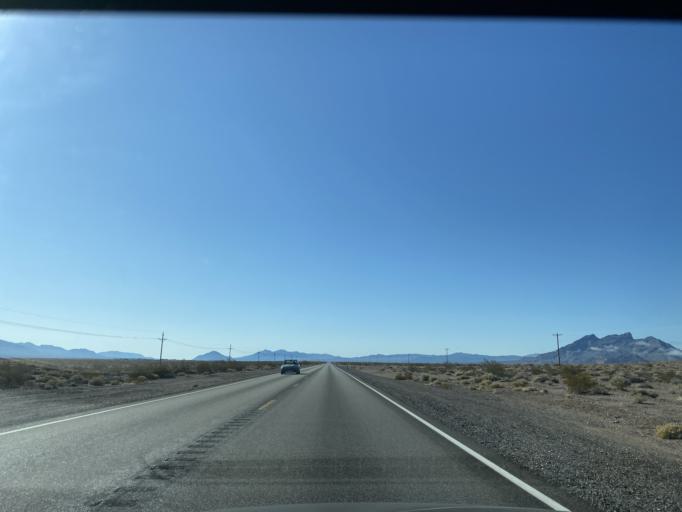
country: US
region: Nevada
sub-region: Nye County
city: Pahrump
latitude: 36.4656
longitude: -116.4218
